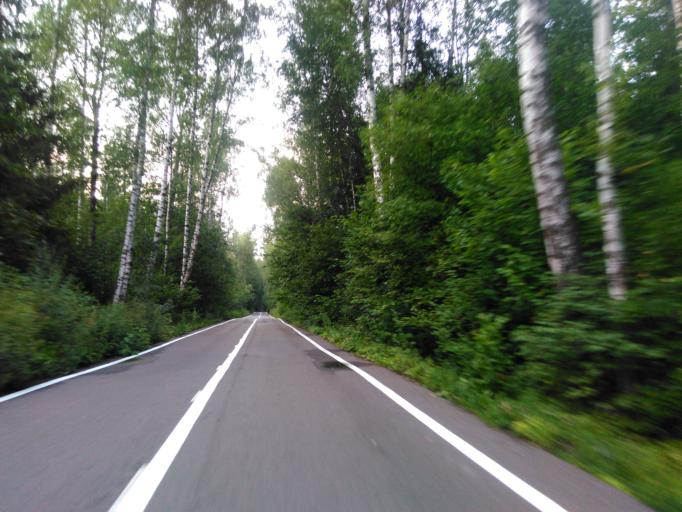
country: RU
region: Moscow
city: Babushkin
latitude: 55.8491
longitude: 37.7258
